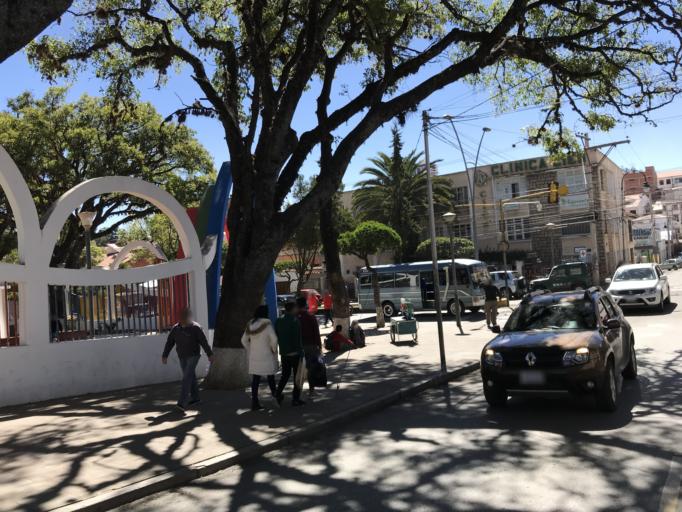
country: BO
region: Chuquisaca
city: Sucre
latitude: -19.0423
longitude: -65.2622
